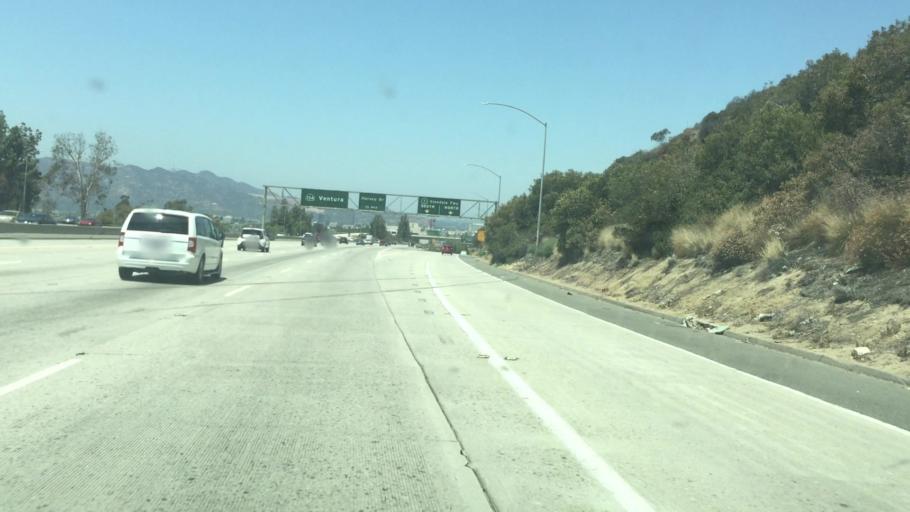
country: US
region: California
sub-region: Los Angeles County
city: Glendale
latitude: 34.1452
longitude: -118.2172
